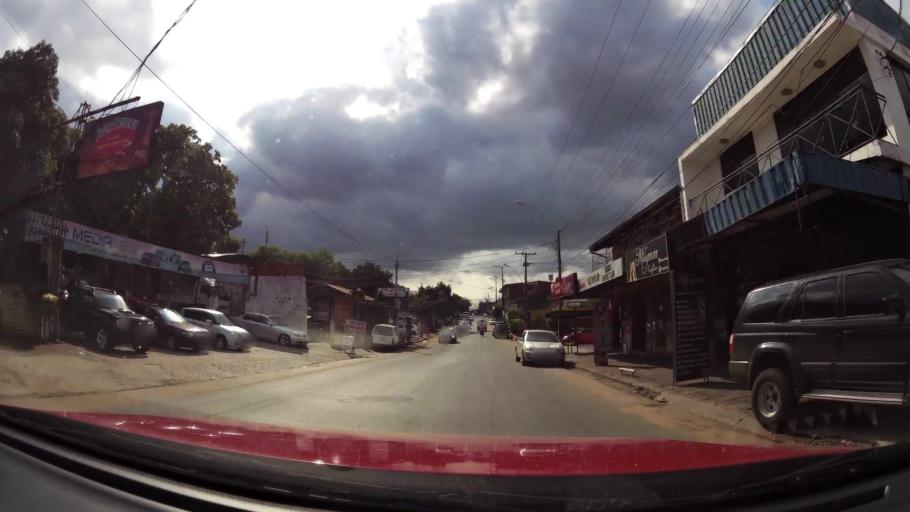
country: PY
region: Central
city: Fernando de la Mora
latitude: -25.3412
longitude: -57.5529
